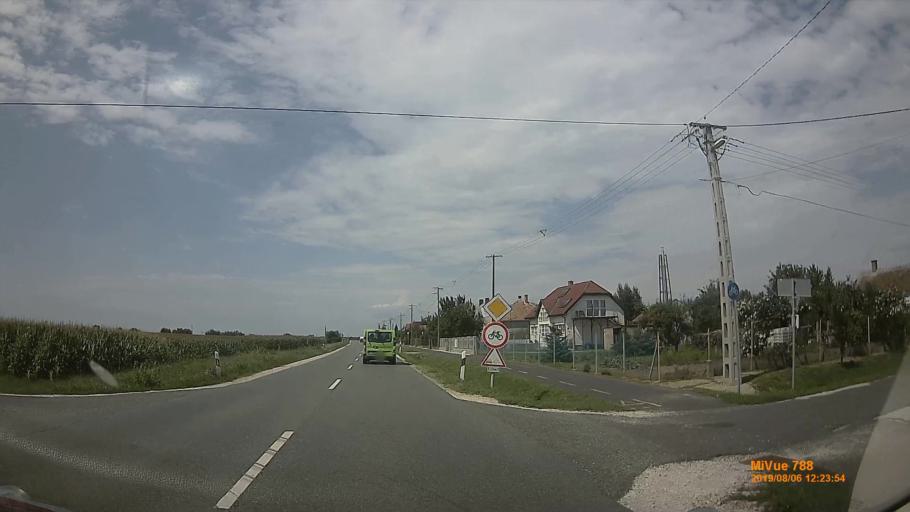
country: HU
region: Vas
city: Taplanszentkereszt
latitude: 47.1911
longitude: 16.7060
